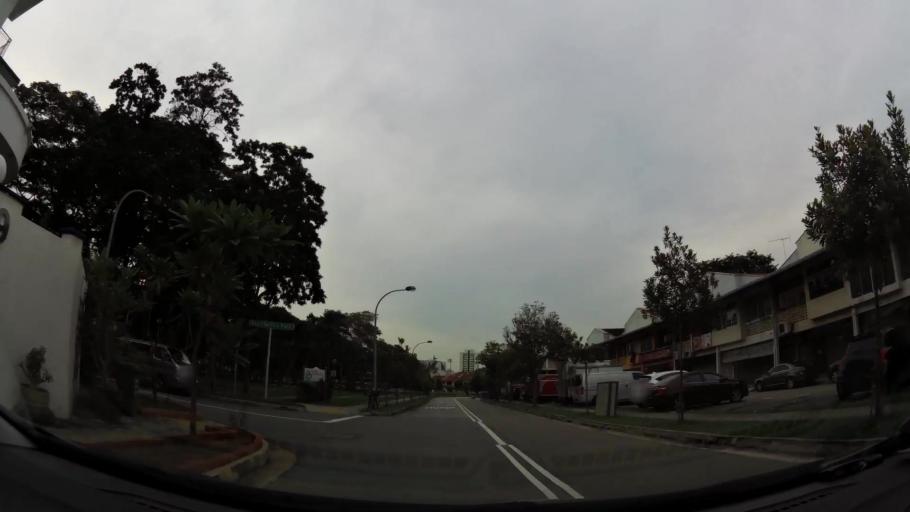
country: SG
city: Singapore
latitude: 1.3673
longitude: 103.8904
